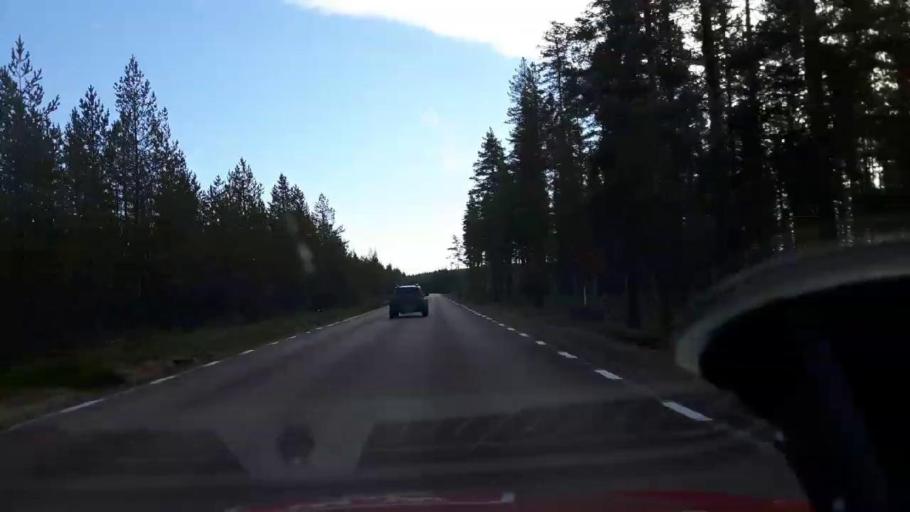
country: SE
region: Gaevleborg
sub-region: Ljusdals Kommun
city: Farila
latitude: 61.9403
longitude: 15.4817
